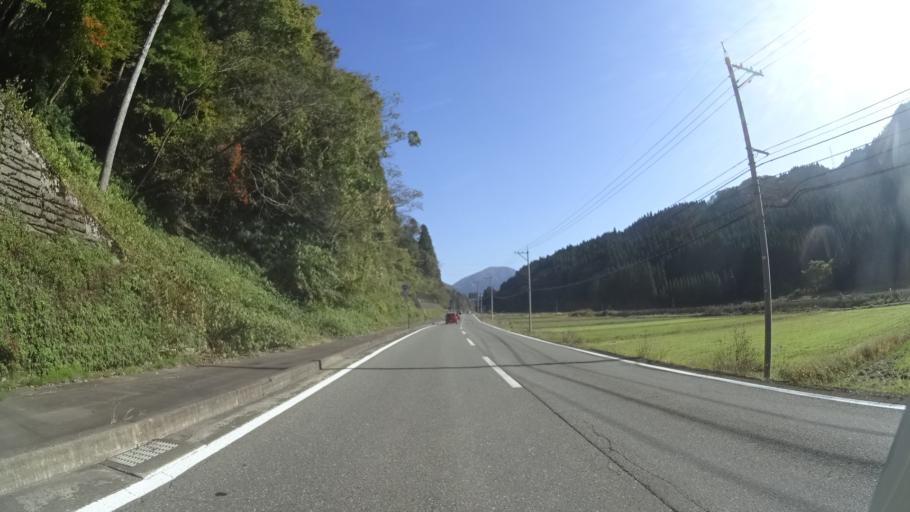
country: JP
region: Fukui
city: Ono
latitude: 36.0078
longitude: 136.3957
